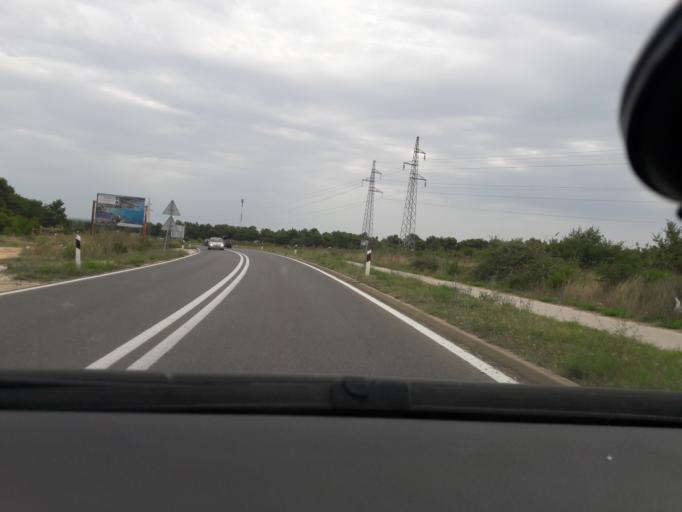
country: HR
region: Zadarska
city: Nin
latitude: 44.2427
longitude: 15.1680
